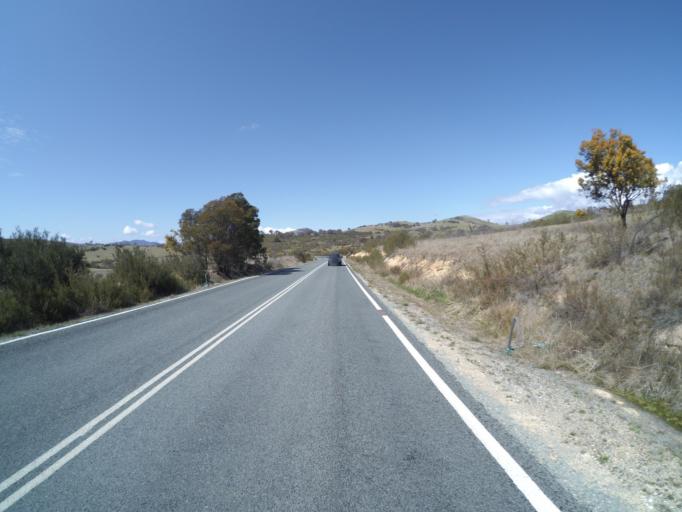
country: AU
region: Australian Capital Territory
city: Macarthur
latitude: -35.4540
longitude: 149.0072
